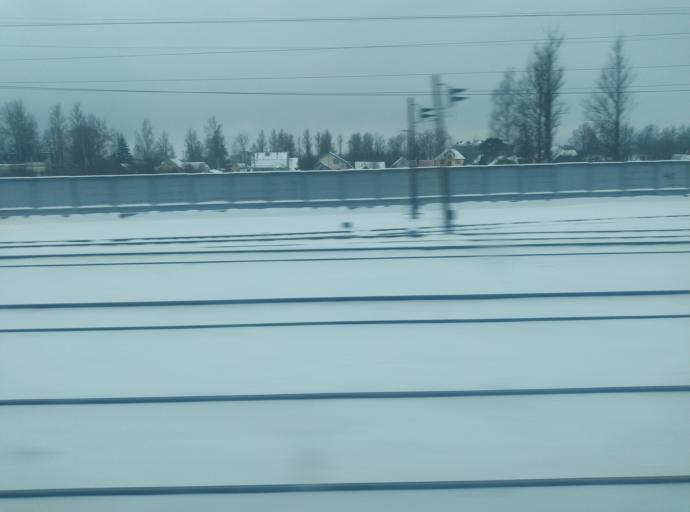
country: RU
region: Leningrad
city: Lyuban'
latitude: 59.3490
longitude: 31.2550
